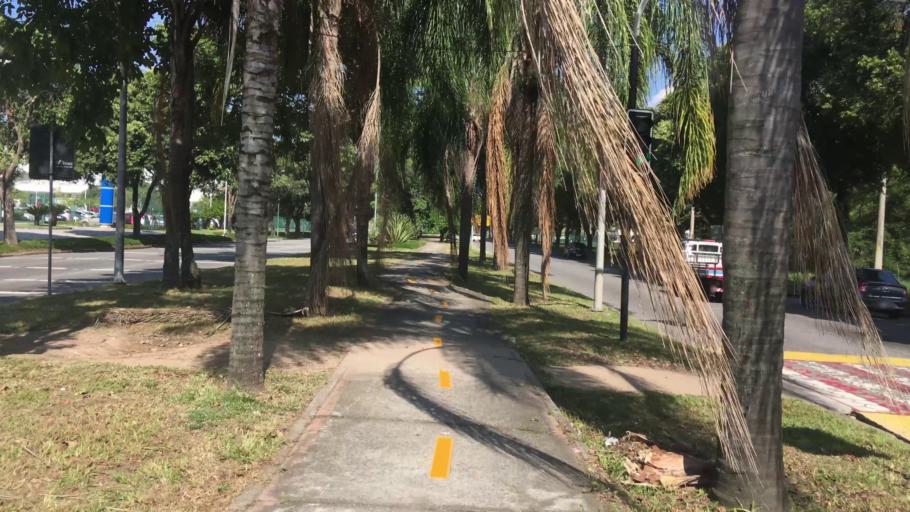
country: BR
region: Rio de Janeiro
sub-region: Rio De Janeiro
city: Rio de Janeiro
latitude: -22.8472
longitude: -43.2358
